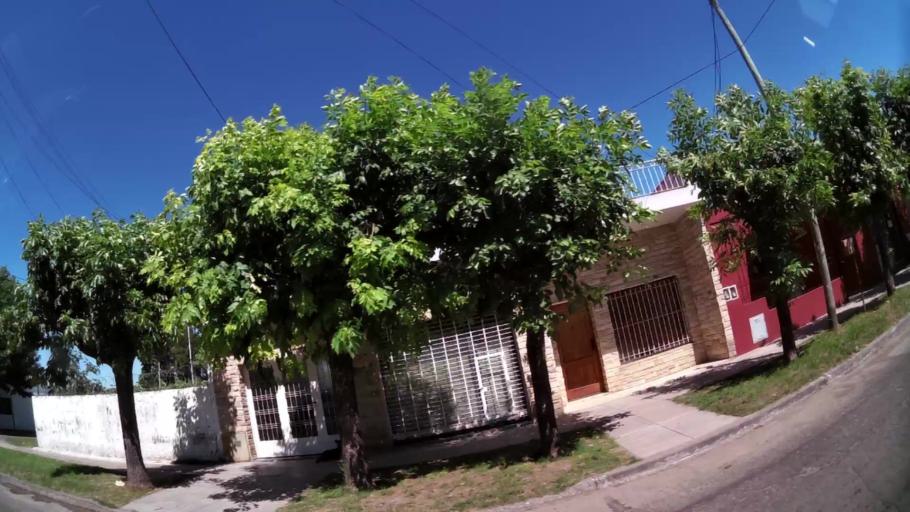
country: AR
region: Buenos Aires
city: Hurlingham
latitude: -34.5097
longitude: -58.6743
